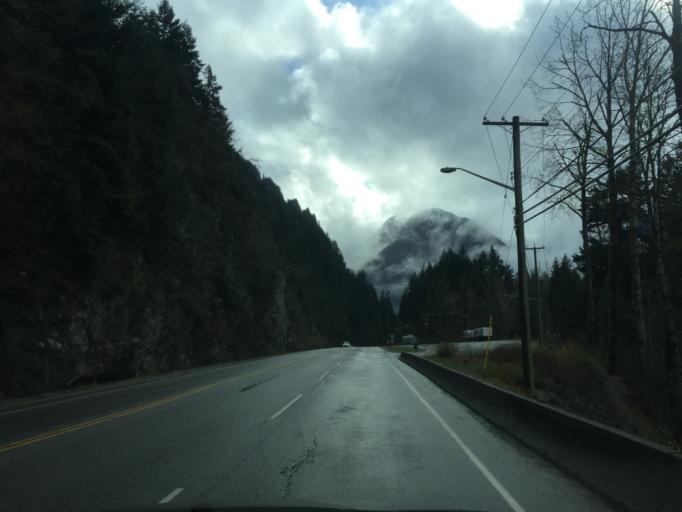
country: CA
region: British Columbia
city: Hope
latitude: 49.3696
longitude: -121.4473
